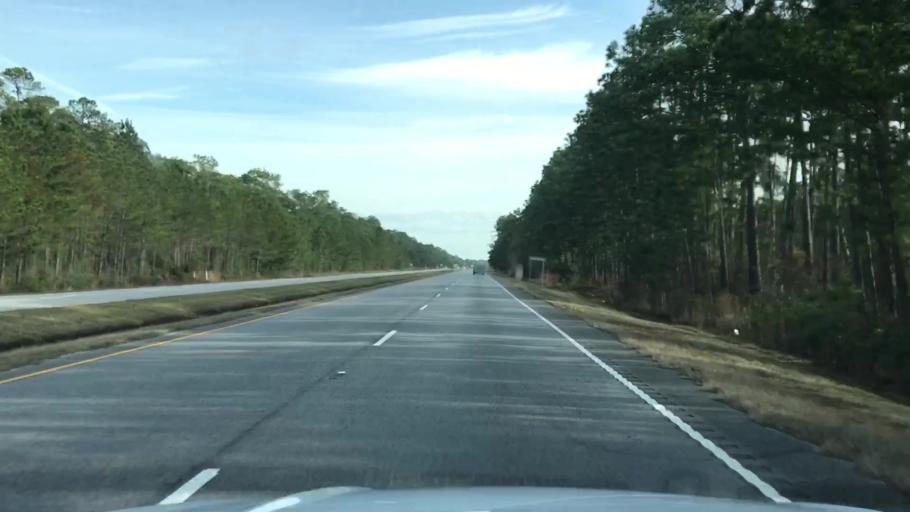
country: US
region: South Carolina
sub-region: Georgetown County
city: Georgetown
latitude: 33.4095
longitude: -79.1922
